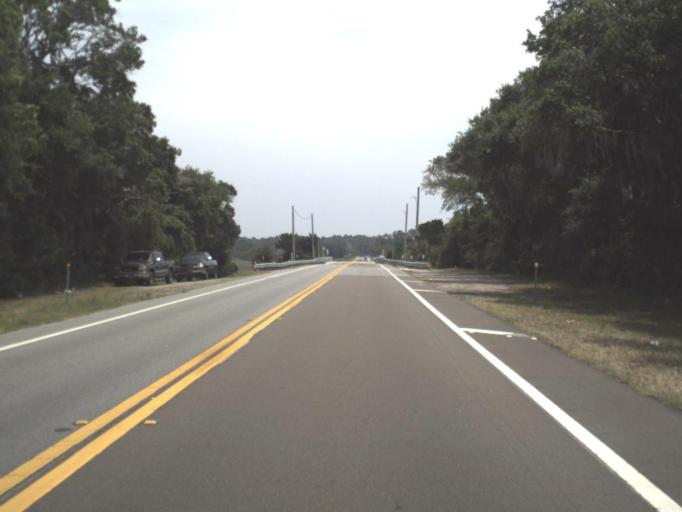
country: US
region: Florida
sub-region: Duval County
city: Atlantic Beach
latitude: 30.4637
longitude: -81.4331
